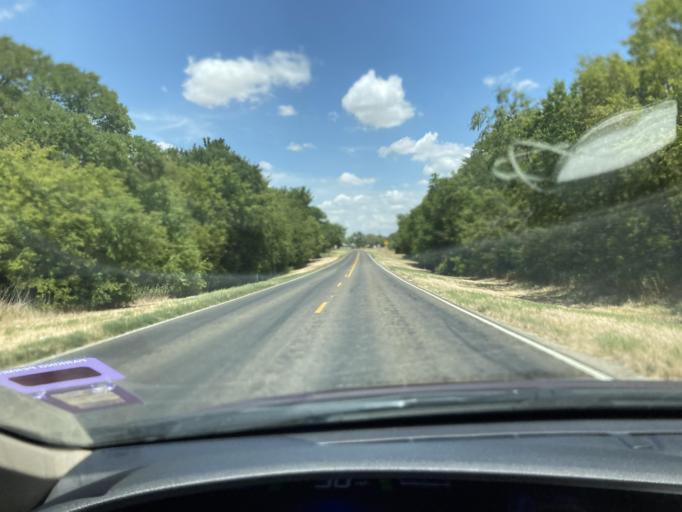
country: US
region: Texas
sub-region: Navarro County
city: Corsicana
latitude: 32.0579
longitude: -96.4985
